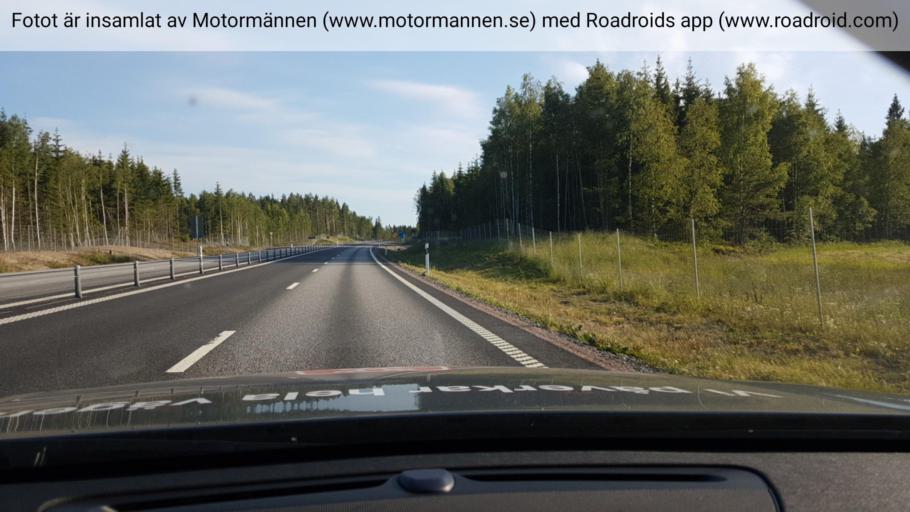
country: SE
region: Uppsala
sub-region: Osthammars Kommun
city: Gimo
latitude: 60.1296
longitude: 18.1541
